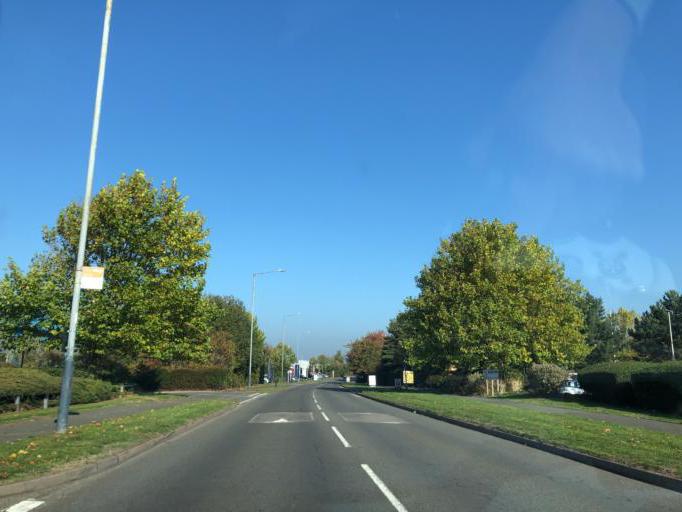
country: GB
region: England
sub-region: Warwickshire
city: Royal Leamington Spa
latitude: 52.2751
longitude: -1.5448
